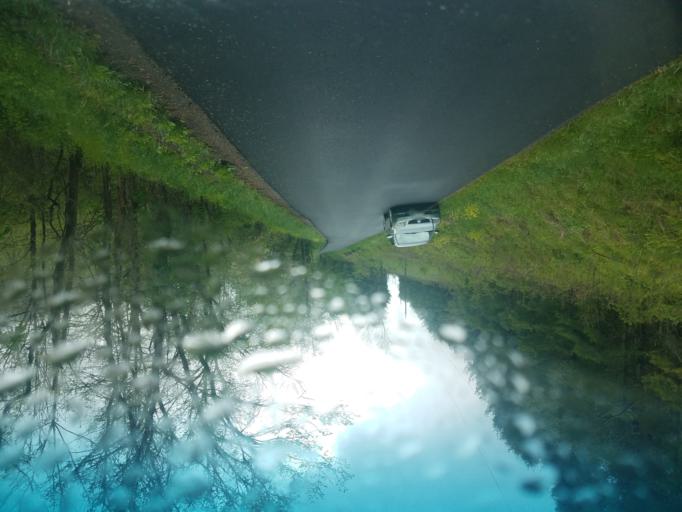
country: US
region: Virginia
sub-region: Smyth County
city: Marion
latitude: 36.9278
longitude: -81.5433
